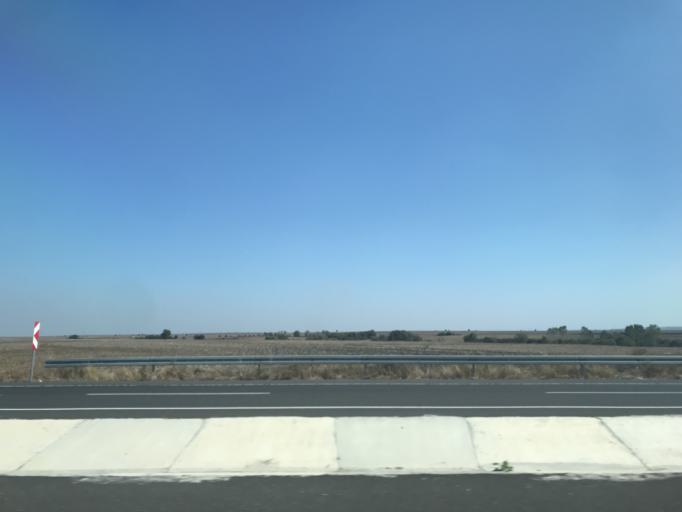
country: TR
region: Tekirdag
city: Muratli
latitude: 41.1827
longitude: 27.5390
